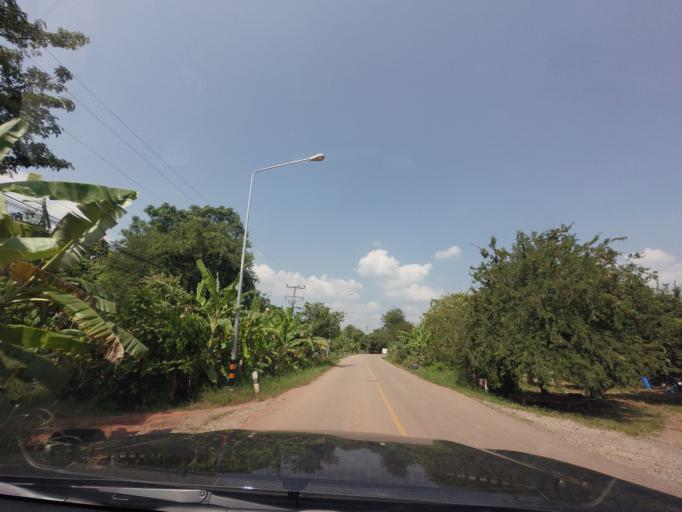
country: TH
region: Uttaradit
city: Fak Tha
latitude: 17.8736
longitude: 100.9736
